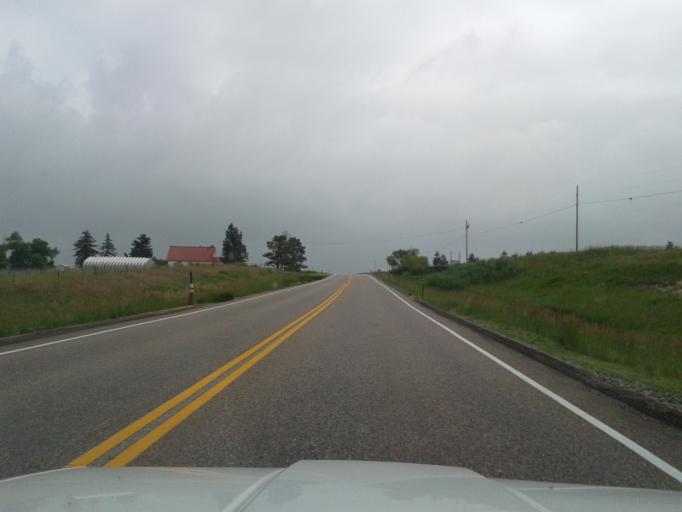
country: US
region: Colorado
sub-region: El Paso County
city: Woodmoor
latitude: 39.1982
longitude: -104.7212
